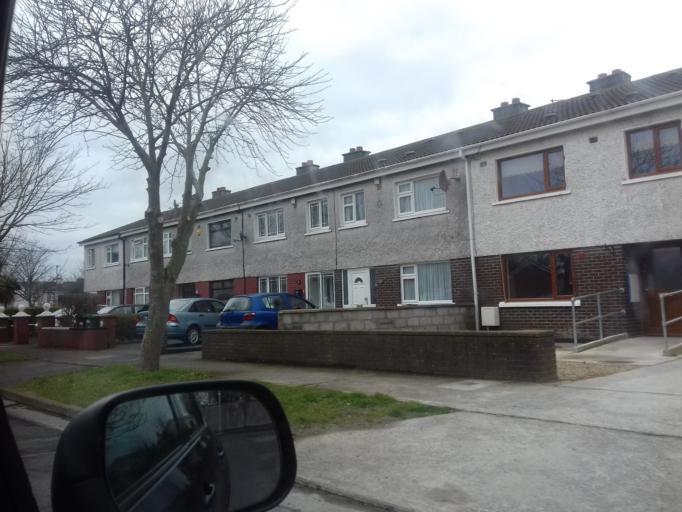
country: IE
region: Leinster
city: Portmarnock
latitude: 53.4214
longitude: -6.1328
